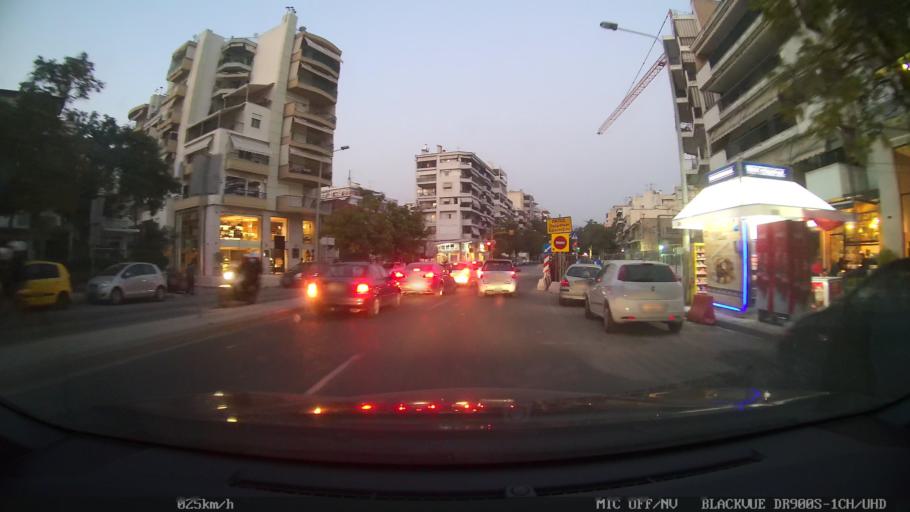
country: GR
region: Central Macedonia
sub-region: Nomos Thessalonikis
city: Kalamaria
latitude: 40.5954
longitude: 22.9598
